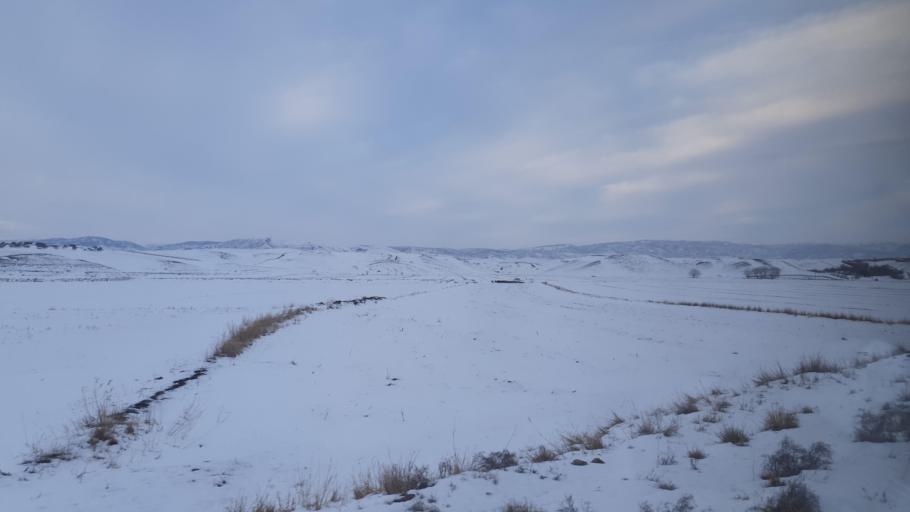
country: TR
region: Kirsehir
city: Mecidiye
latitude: 39.6861
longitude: 34.4040
